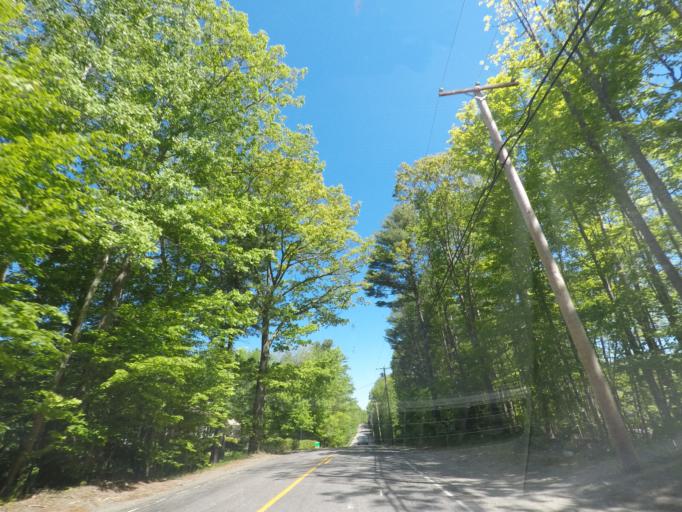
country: US
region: Maine
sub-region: Kennebec County
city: Manchester
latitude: 44.2868
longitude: -69.8893
